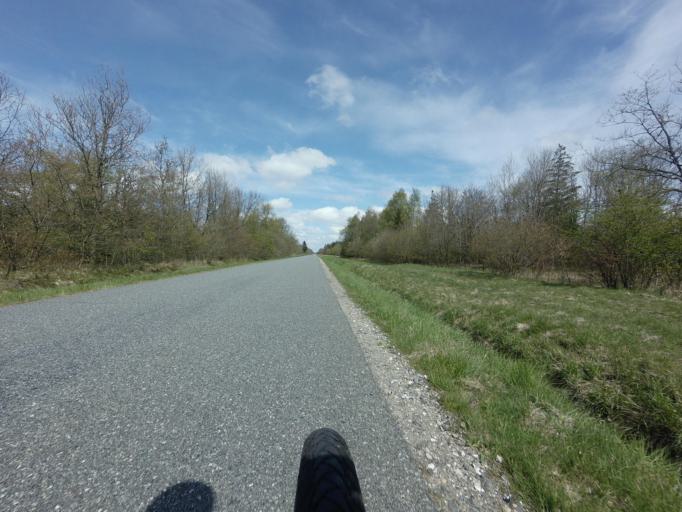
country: DK
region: North Denmark
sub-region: Jammerbugt Kommune
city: Brovst
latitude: 57.1666
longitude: 9.5432
